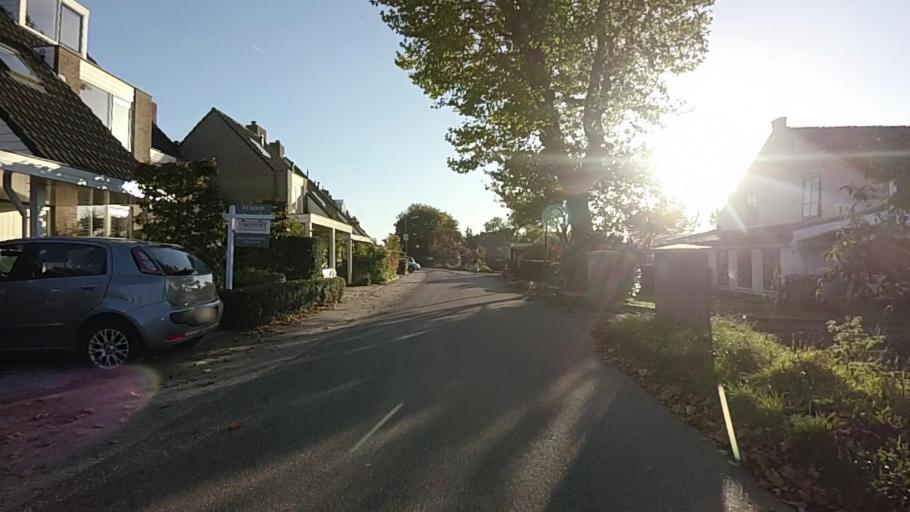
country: NL
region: Utrecht
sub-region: Stichtse Vecht
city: Vreeland
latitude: 52.2354
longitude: 5.0312
